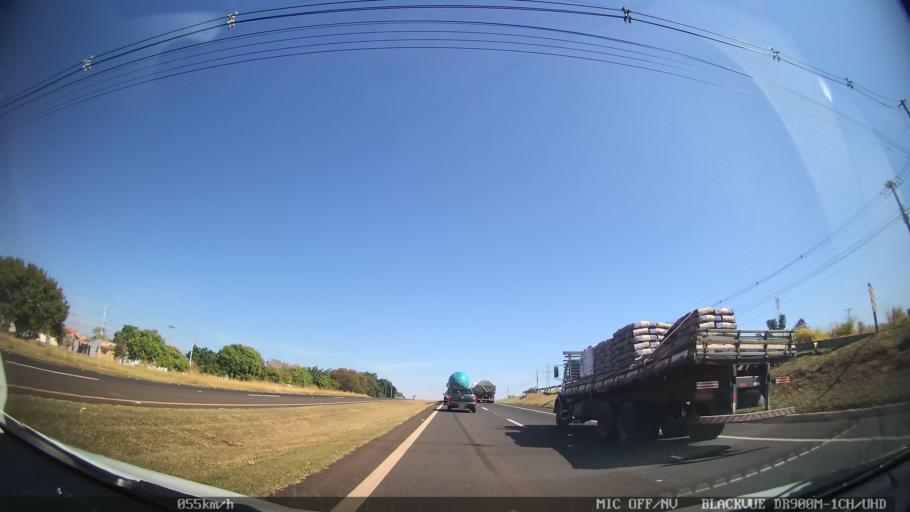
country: BR
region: Sao Paulo
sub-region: Ribeirao Preto
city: Ribeirao Preto
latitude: -21.1293
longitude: -47.8487
